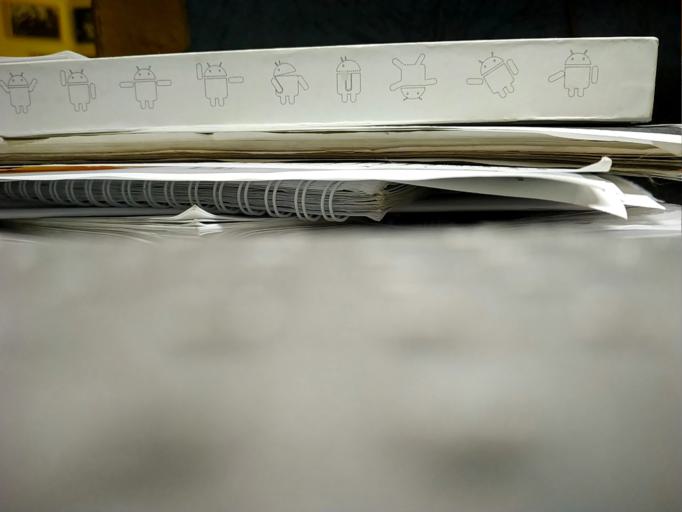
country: EE
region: Ida-Virumaa
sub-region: Narva linn
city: Narva
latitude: 59.4584
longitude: 28.2199
